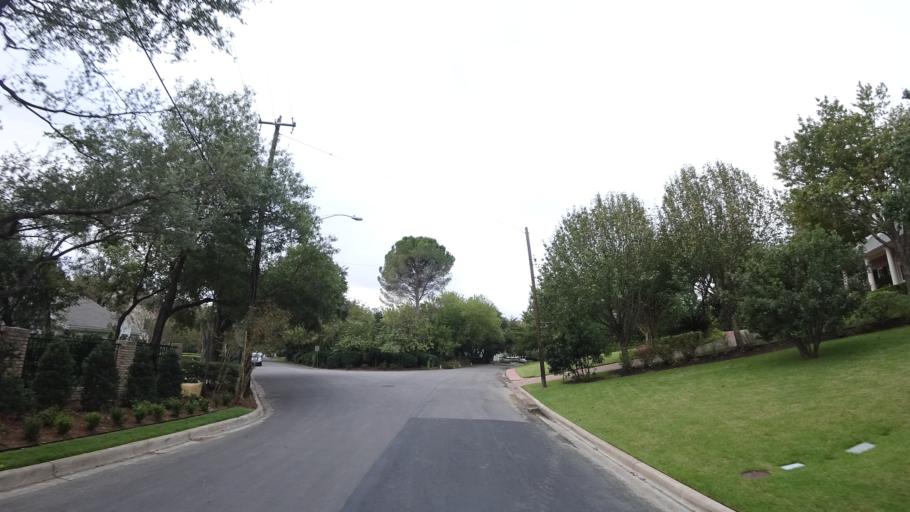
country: US
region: Texas
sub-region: Travis County
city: Austin
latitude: 30.2959
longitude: -97.7506
